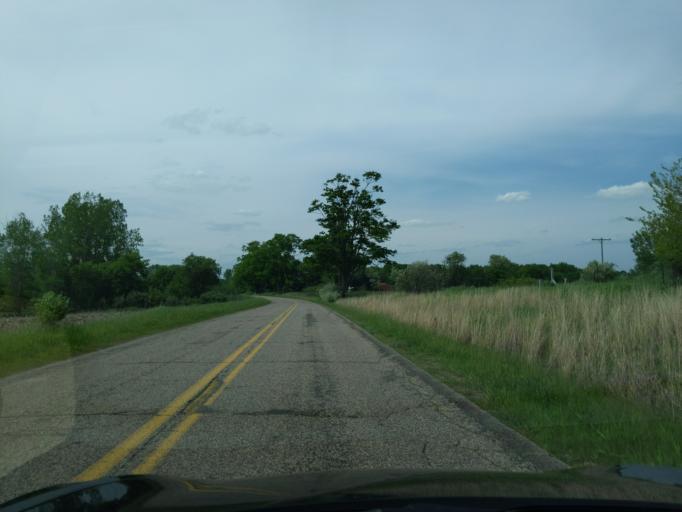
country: US
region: Michigan
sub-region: Ingham County
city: Leslie
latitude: 42.4225
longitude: -84.3336
